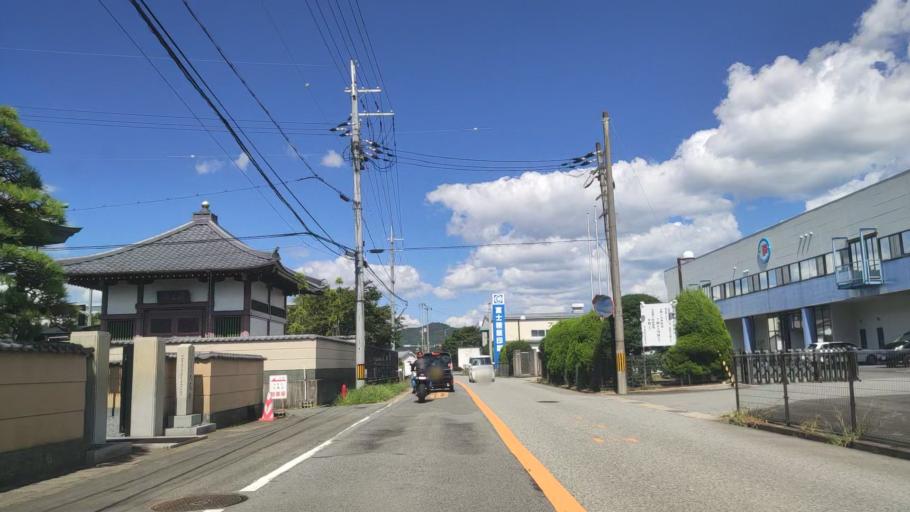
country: JP
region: Kyoto
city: Fukuchiyama
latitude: 35.2232
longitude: 135.1301
